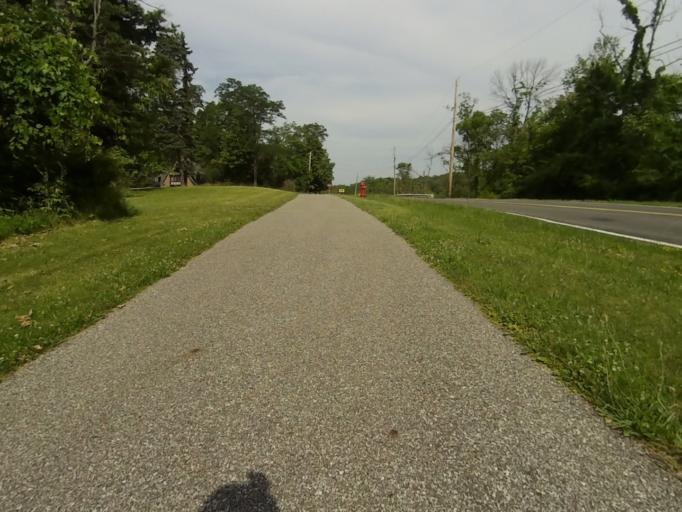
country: US
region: Ohio
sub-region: Summit County
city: Boston Heights
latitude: 41.2750
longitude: -81.5357
